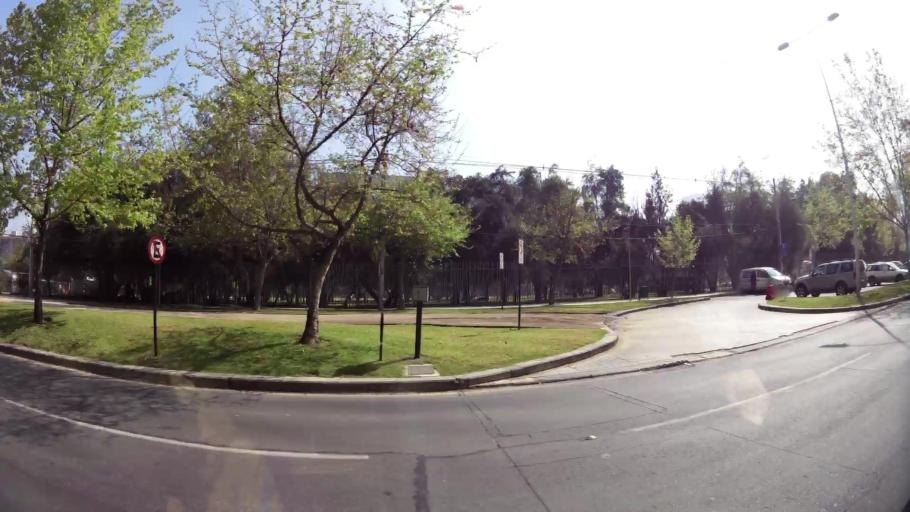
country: CL
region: Santiago Metropolitan
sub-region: Provincia de Santiago
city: Villa Presidente Frei, Nunoa, Santiago, Chile
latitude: -33.4052
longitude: -70.5768
